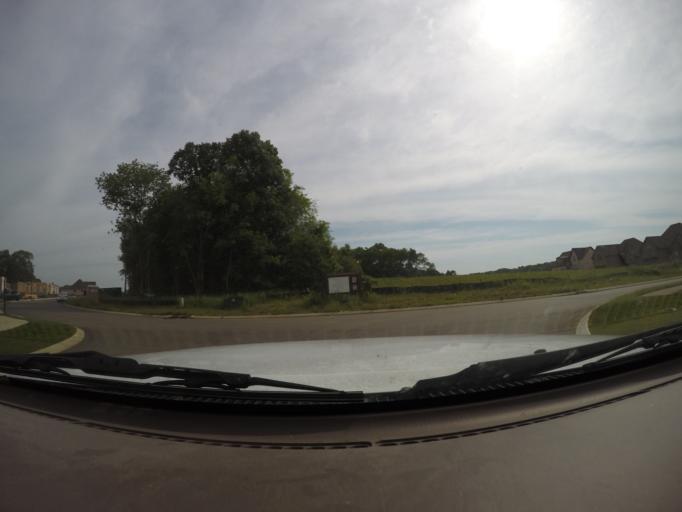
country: US
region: Tennessee
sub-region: Wilson County
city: Mount Juliet
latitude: 36.2196
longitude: -86.4866
